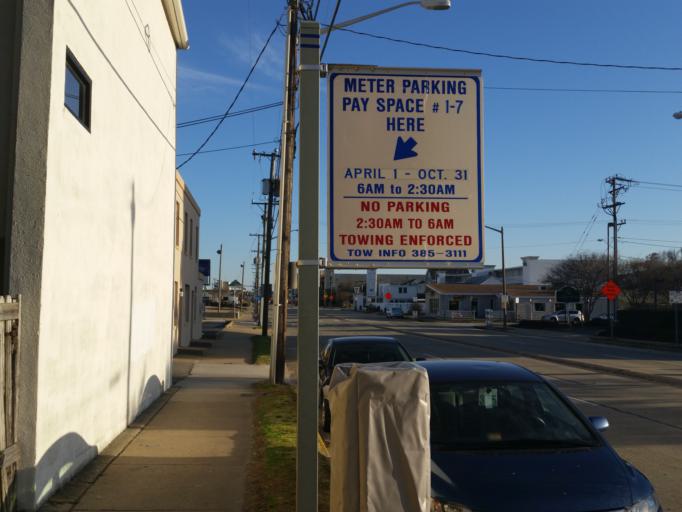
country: US
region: Virginia
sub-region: City of Virginia Beach
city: Virginia Beach
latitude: 36.8569
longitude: -75.9786
